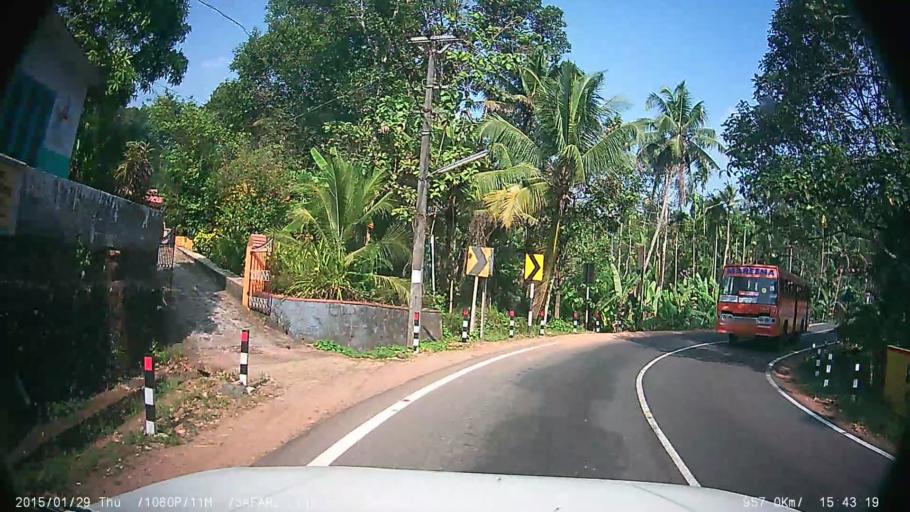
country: IN
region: Kerala
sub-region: Kottayam
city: Kottayam
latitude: 9.5367
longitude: 76.5661
